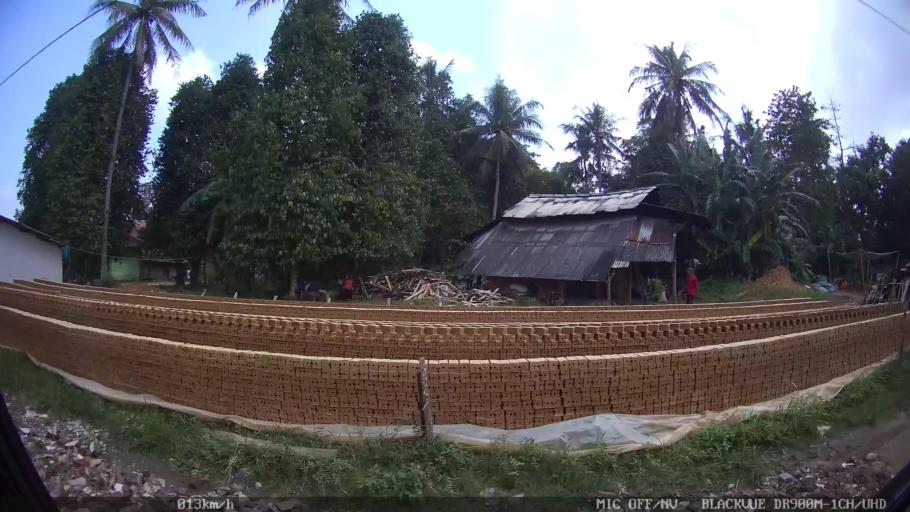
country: ID
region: Lampung
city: Kedaton
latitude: -5.3315
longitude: 105.2884
